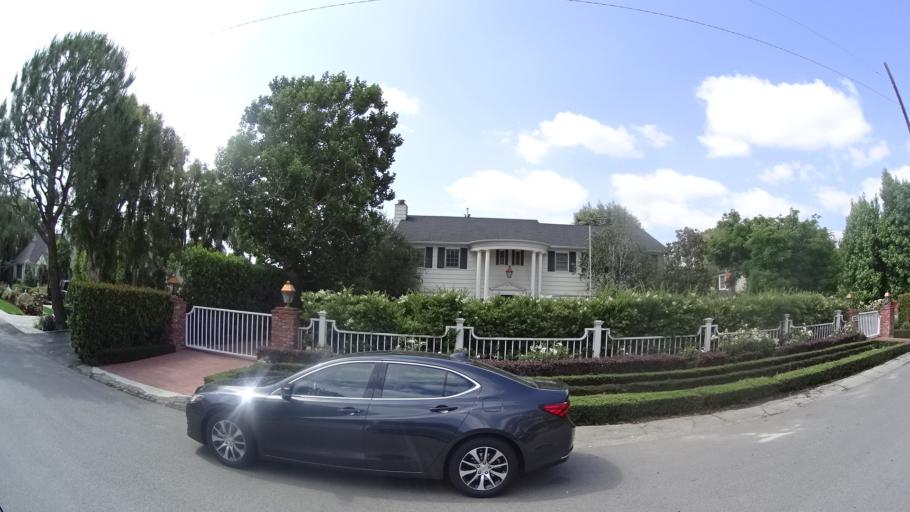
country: US
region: California
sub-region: Los Angeles County
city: Universal City
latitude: 34.1558
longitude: -118.3584
